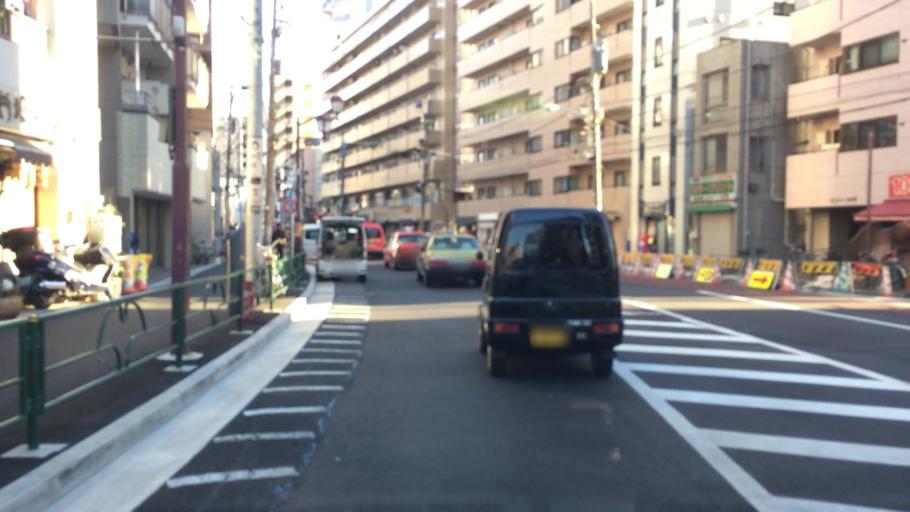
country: JP
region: Tokyo
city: Tokyo
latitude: 35.7211
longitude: 139.7622
